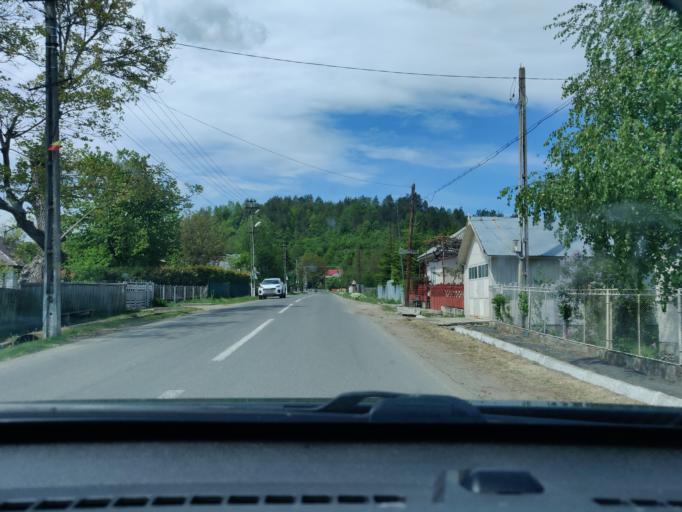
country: RO
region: Vrancea
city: Dragosloveni
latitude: 46.0040
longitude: 26.6732
